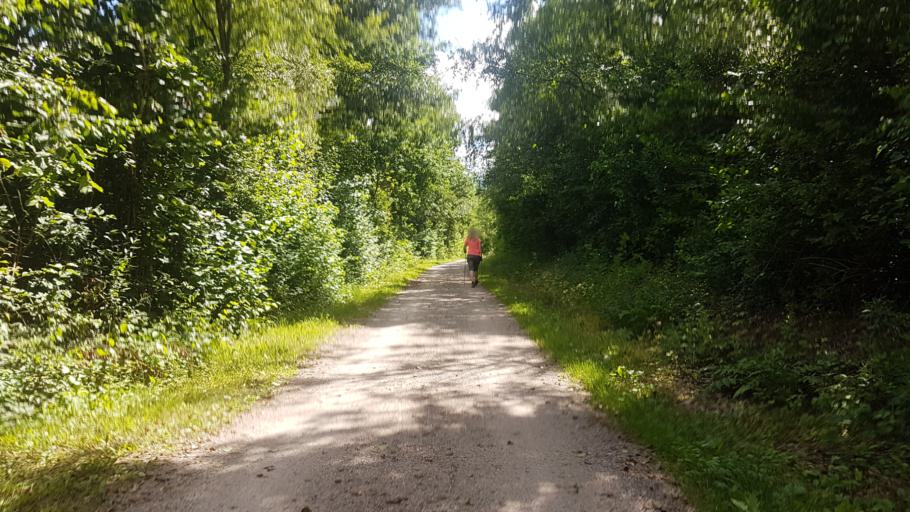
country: DE
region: Bavaria
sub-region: Regierungsbezirk Mittelfranken
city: Gunzenhausen
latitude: 49.1272
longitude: 10.7751
